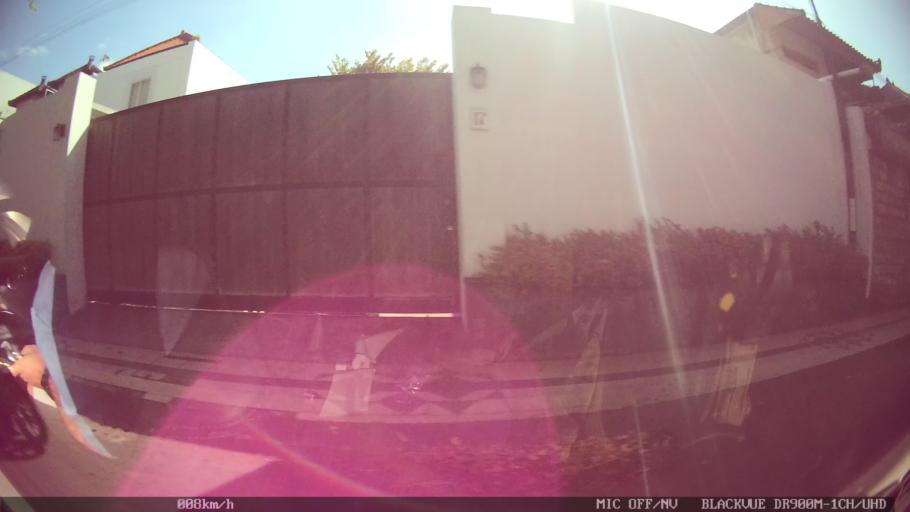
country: ID
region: Bali
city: Jabajero
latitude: -8.7277
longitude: 115.1778
